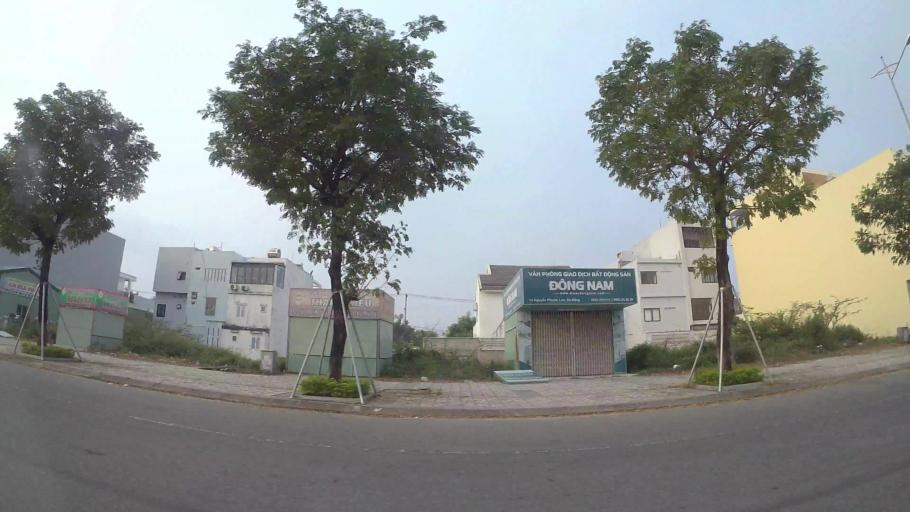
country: VN
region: Da Nang
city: Cam Le
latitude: 16.0212
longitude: 108.2264
